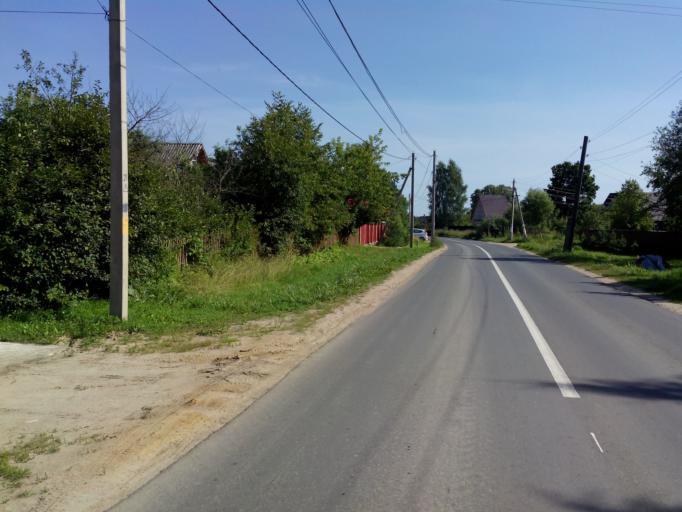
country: RU
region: Moskovskaya
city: Verbilki
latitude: 56.5433
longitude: 37.6142
